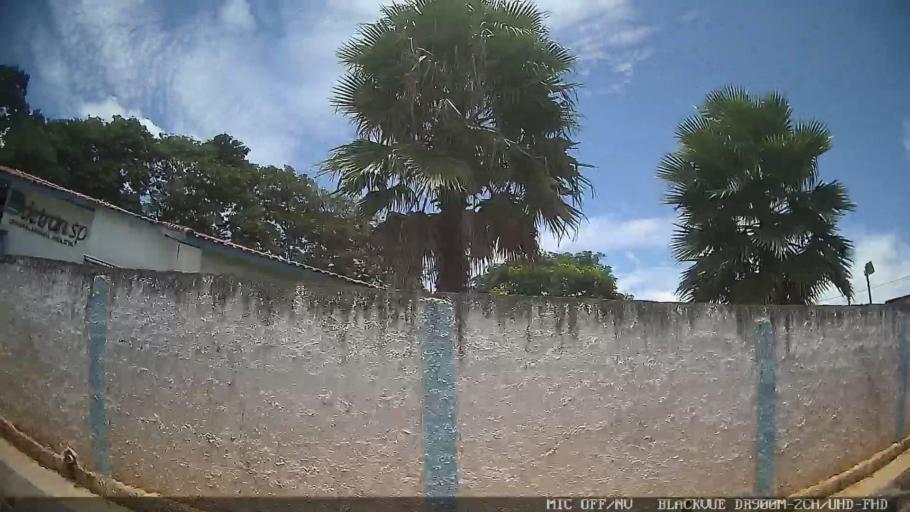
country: BR
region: Sao Paulo
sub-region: Laranjal Paulista
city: Laranjal Paulista
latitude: -23.0515
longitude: -47.8275
